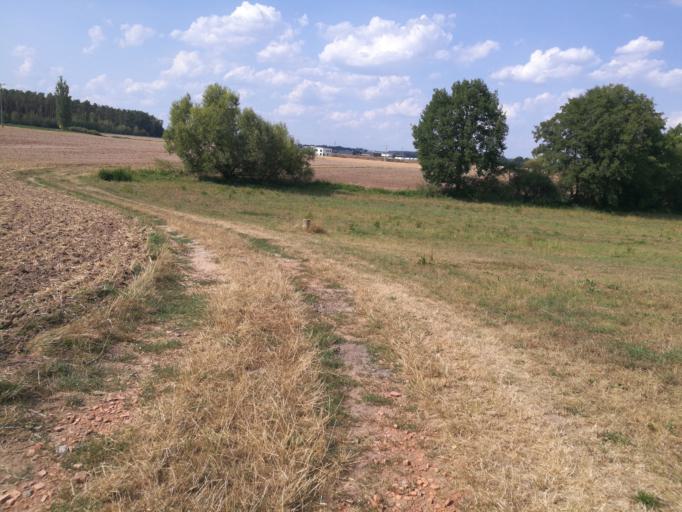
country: DE
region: Bavaria
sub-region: Regierungsbezirk Mittelfranken
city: Seukendorf
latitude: 49.4973
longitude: 10.8844
